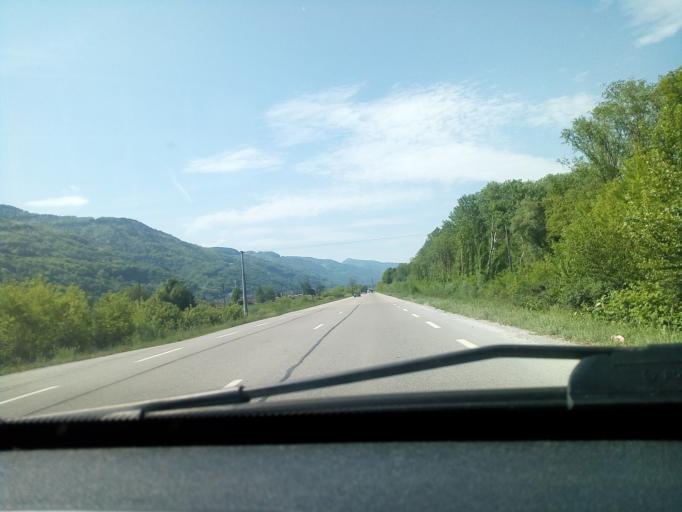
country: FR
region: Rhone-Alpes
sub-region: Departement de l'Isere
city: Froges
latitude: 45.2769
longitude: 5.9185
